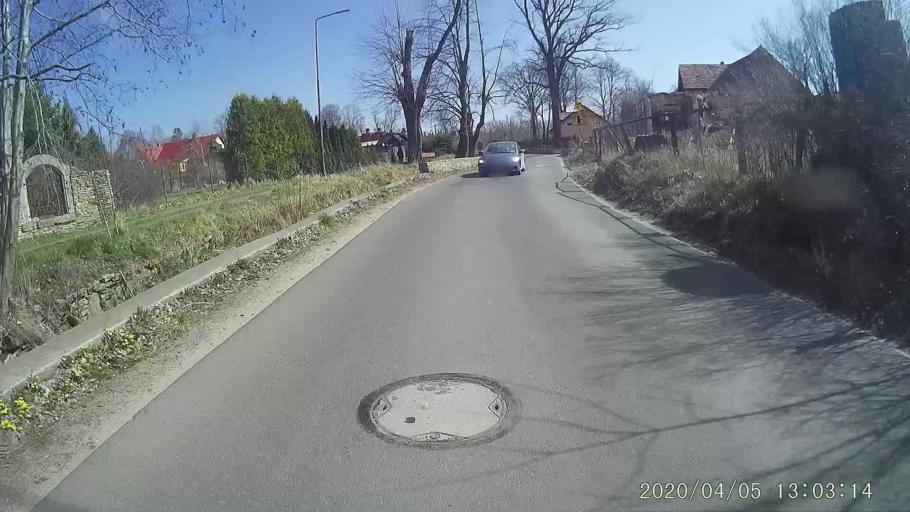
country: PL
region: Lower Silesian Voivodeship
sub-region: Powiat lwowecki
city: Mirsk
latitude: 50.9767
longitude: 15.3555
